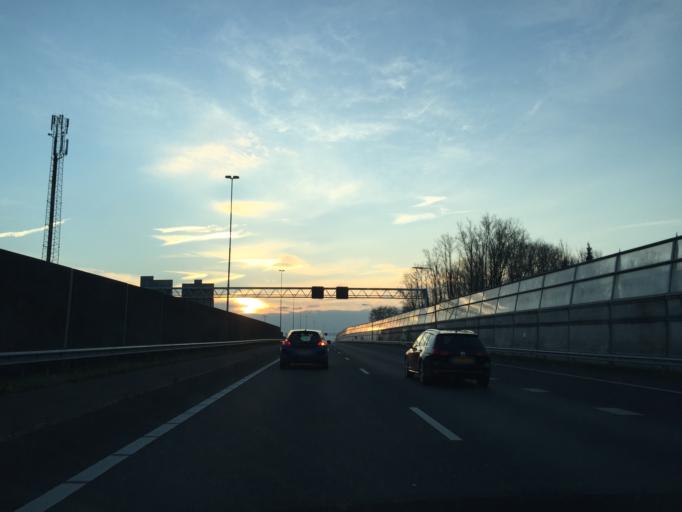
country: NL
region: South Holland
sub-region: Gemeente Hardinxveld-Giessendam
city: Neder-Hardinxveld
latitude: 51.8235
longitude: 4.8387
